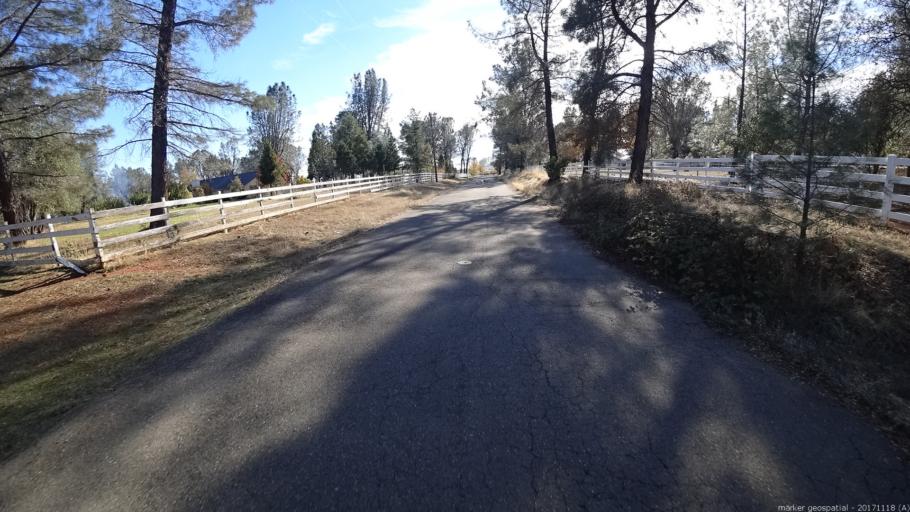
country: US
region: California
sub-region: Shasta County
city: Redding
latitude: 40.4800
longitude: -122.4435
